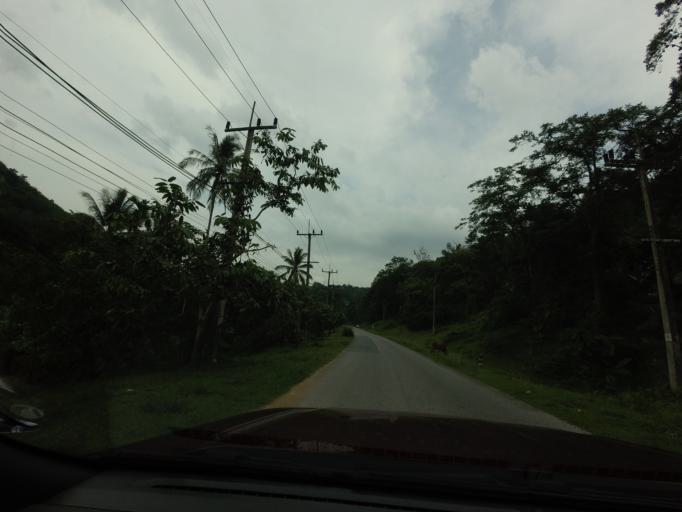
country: TH
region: Yala
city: Than To
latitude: 6.1662
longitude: 101.2681
